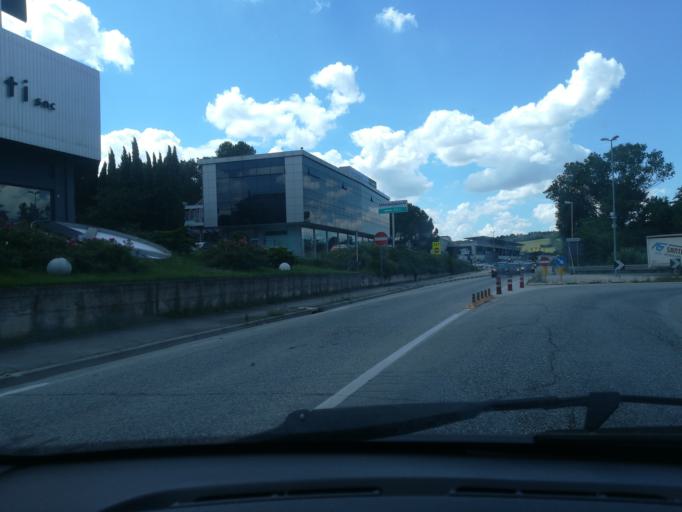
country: IT
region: The Marches
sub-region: Provincia di Macerata
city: Zona Industriale
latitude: 43.2650
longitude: 13.4898
